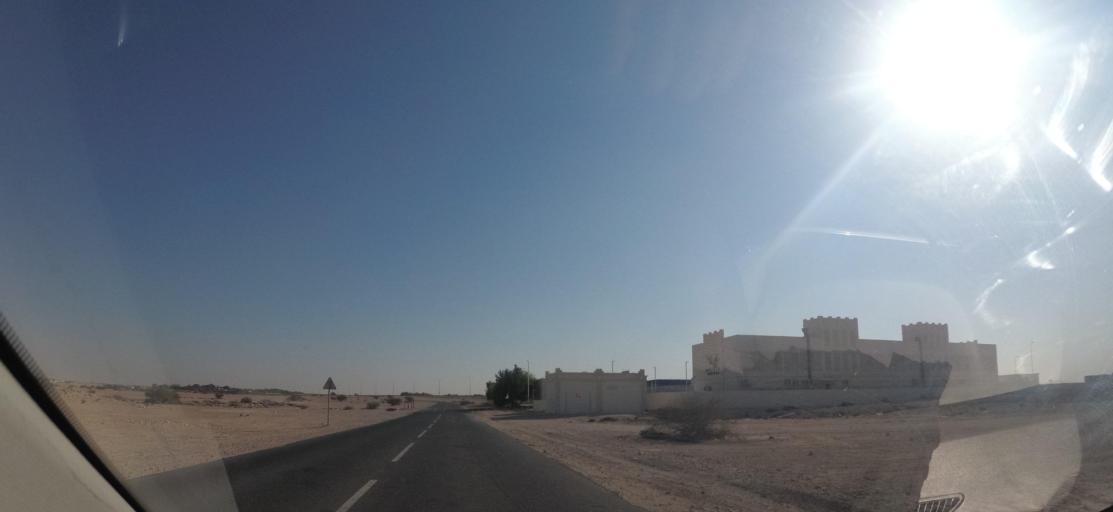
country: QA
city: Al Jumayliyah
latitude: 25.6183
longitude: 51.0861
